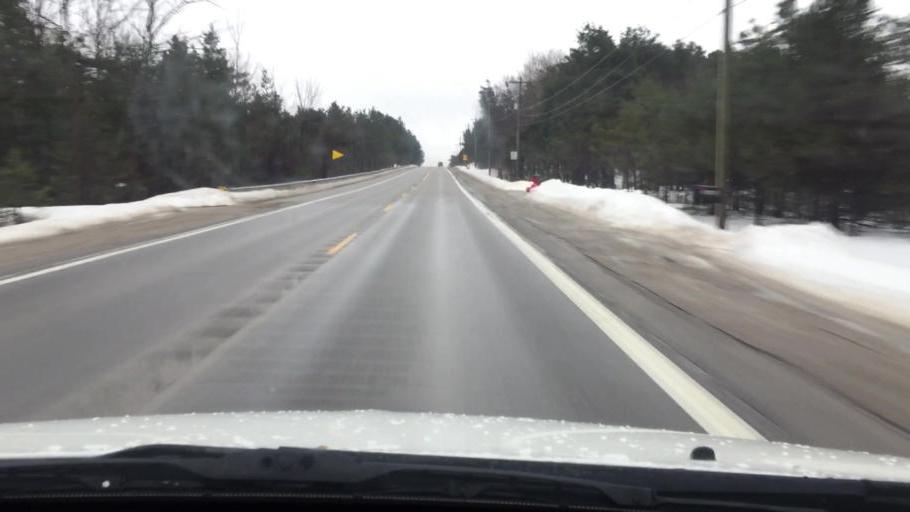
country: US
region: Michigan
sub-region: Charlevoix County
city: Charlevoix
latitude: 45.2683
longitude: -85.2069
